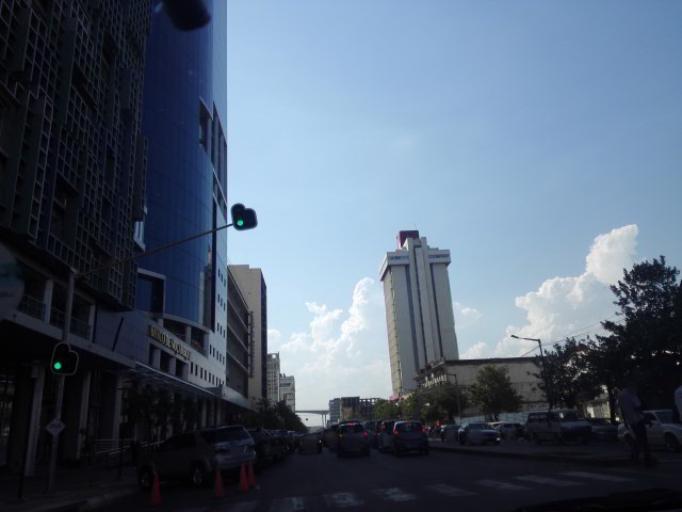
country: MZ
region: Maputo City
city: Maputo
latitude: -25.9729
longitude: 32.5709
